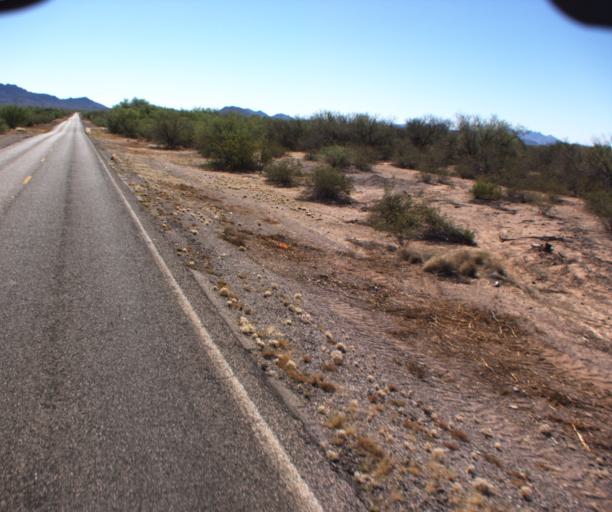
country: US
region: Arizona
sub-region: Pima County
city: Ajo
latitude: 32.3334
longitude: -112.7888
